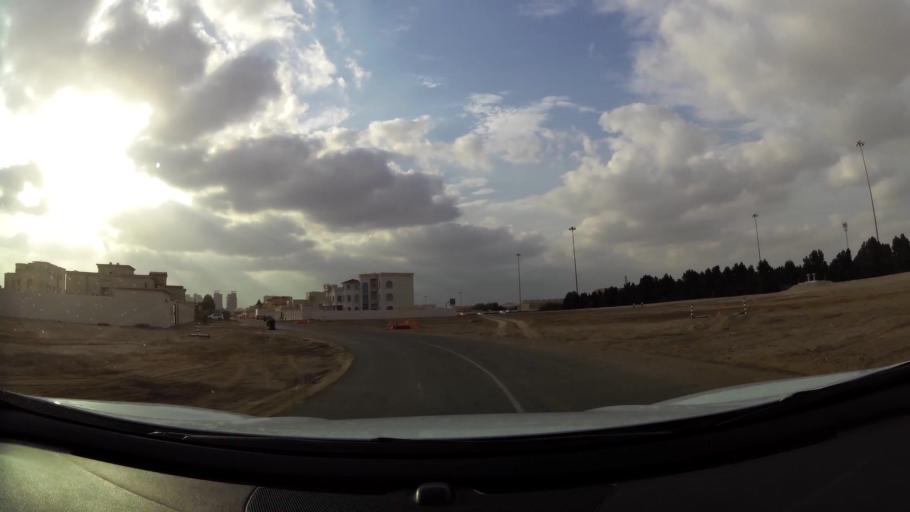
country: AE
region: Abu Dhabi
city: Abu Dhabi
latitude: 24.3734
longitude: 54.5491
